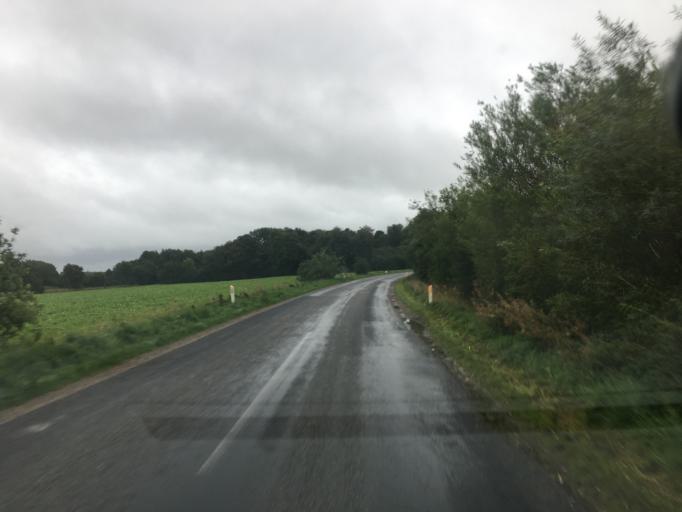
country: DE
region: Schleswig-Holstein
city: Bramstedtlund
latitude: 54.9598
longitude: 9.0525
